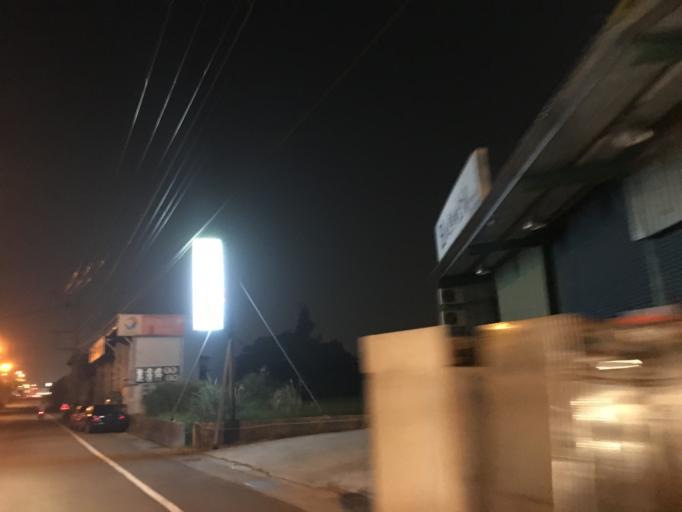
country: TW
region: Taiwan
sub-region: Hsinchu
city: Hsinchu
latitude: 24.6961
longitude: 120.8854
